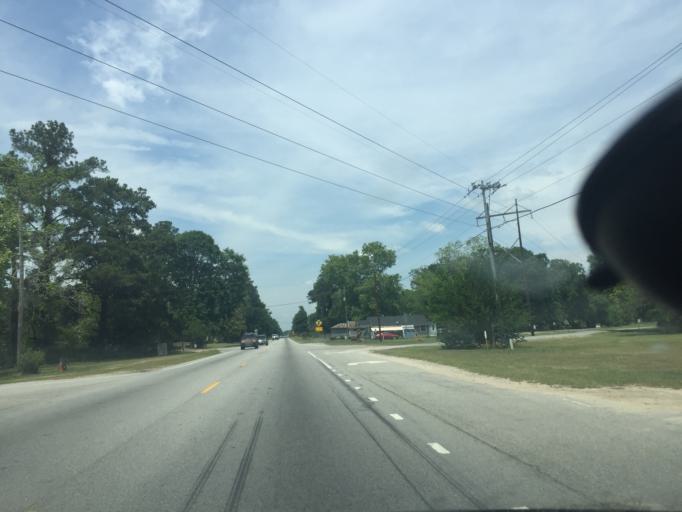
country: US
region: Georgia
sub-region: Chatham County
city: Bloomingdale
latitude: 32.1722
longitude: -81.3892
